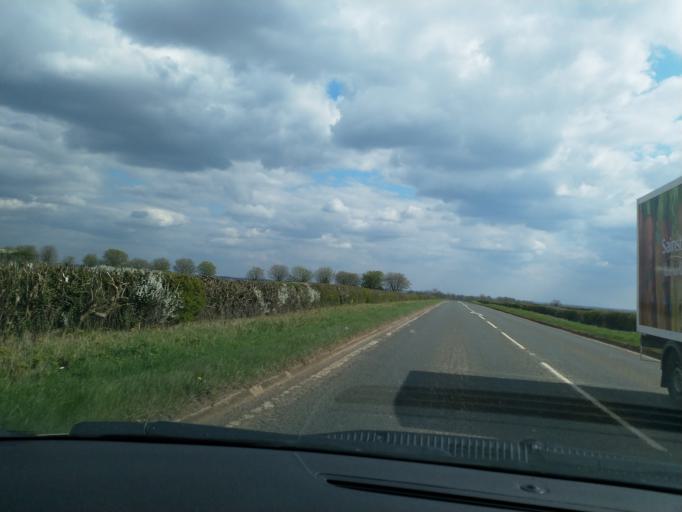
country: GB
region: England
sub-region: Oxfordshire
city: Hanwell
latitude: 52.1118
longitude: -1.3962
